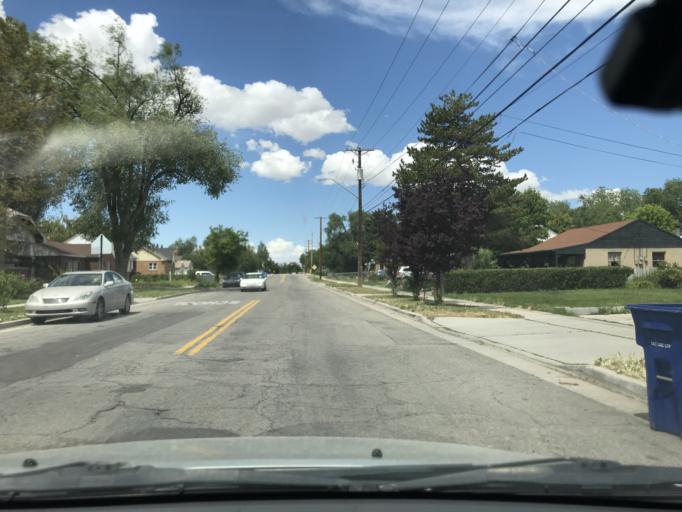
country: US
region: Utah
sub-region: Salt Lake County
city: Salt Lake City
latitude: 40.7802
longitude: -111.9360
